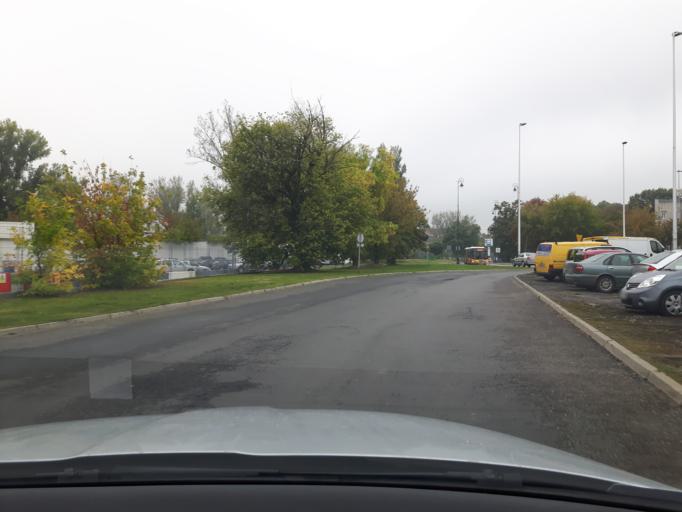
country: PL
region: Masovian Voivodeship
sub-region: Warszawa
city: Praga Polnoc
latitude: 52.2637
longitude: 21.0492
